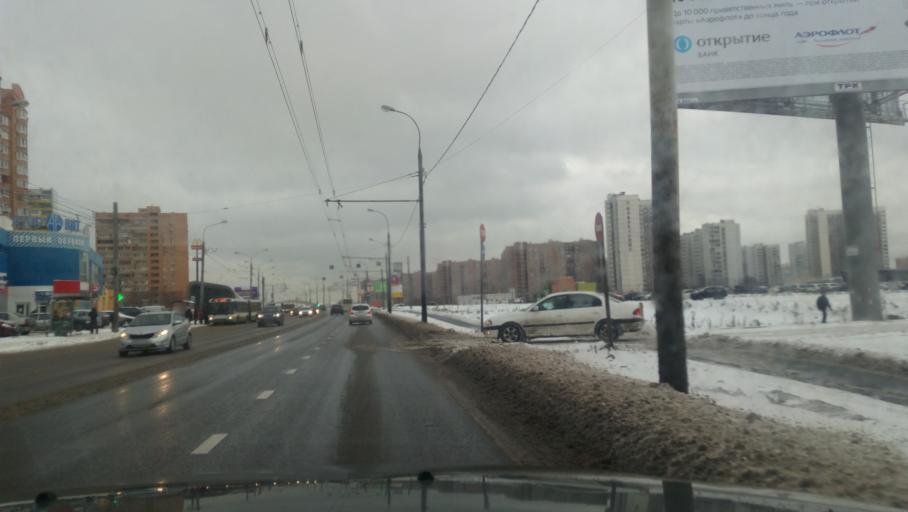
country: RU
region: Moskovskaya
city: Reutov
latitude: 55.7451
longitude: 37.8592
